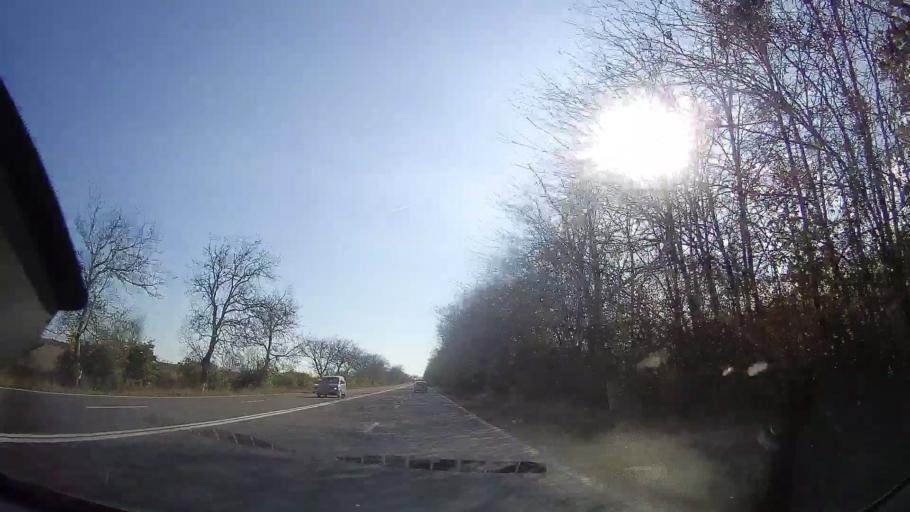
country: RO
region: Constanta
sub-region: Comuna Douazeci si Trei August
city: Douazeci si Trei August
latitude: 43.8922
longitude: 28.5722
